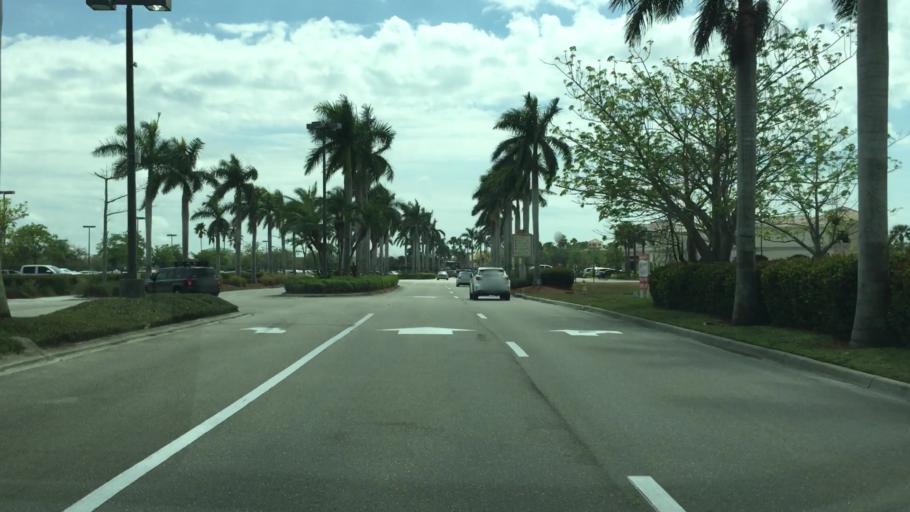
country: US
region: Florida
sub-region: Lee County
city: Three Oaks
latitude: 26.4909
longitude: -81.7873
